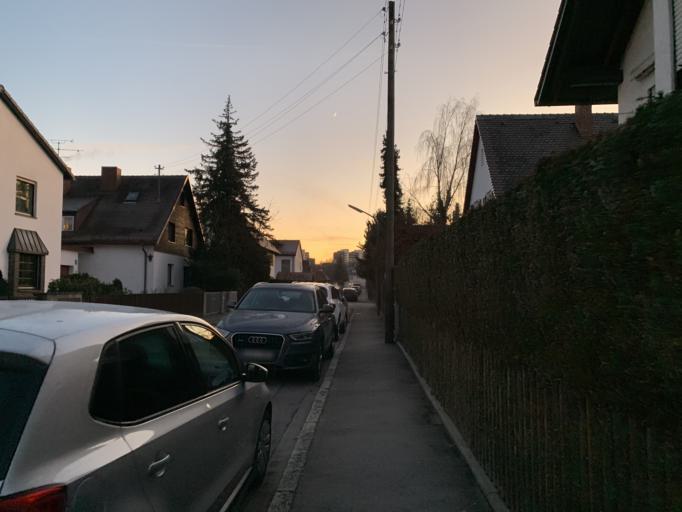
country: DE
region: Bavaria
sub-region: Upper Bavaria
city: Neubiberg
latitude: 48.1122
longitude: 11.6594
